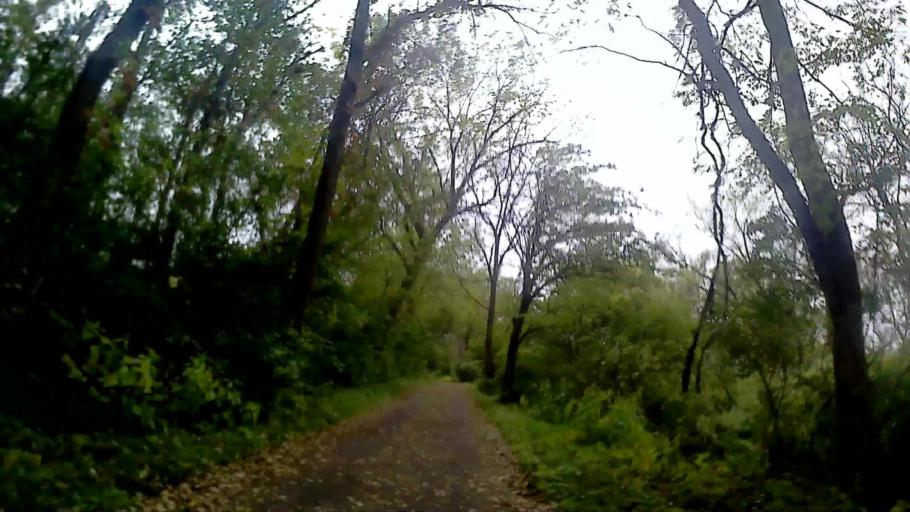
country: US
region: Illinois
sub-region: Kane County
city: Sugar Grove
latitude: 41.7785
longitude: -88.4278
